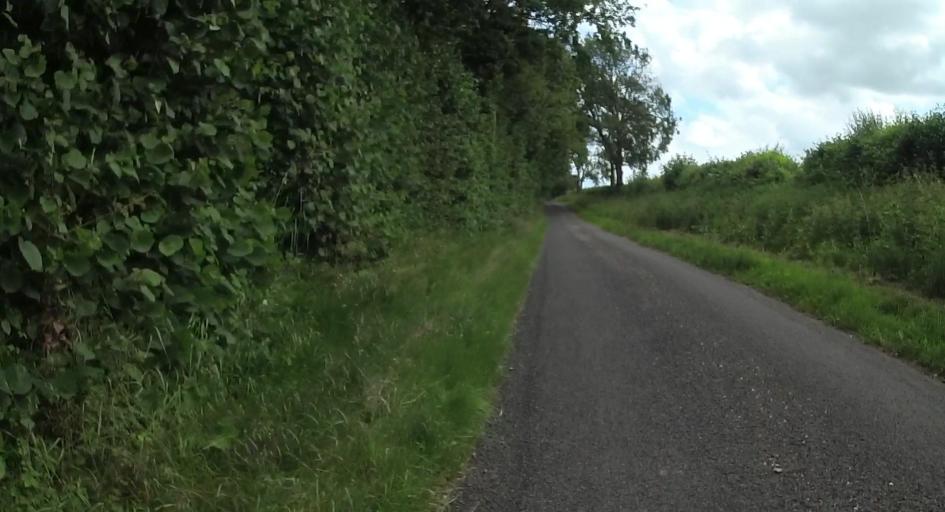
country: GB
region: England
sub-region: Hampshire
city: Four Marks
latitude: 51.1526
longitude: -1.1559
